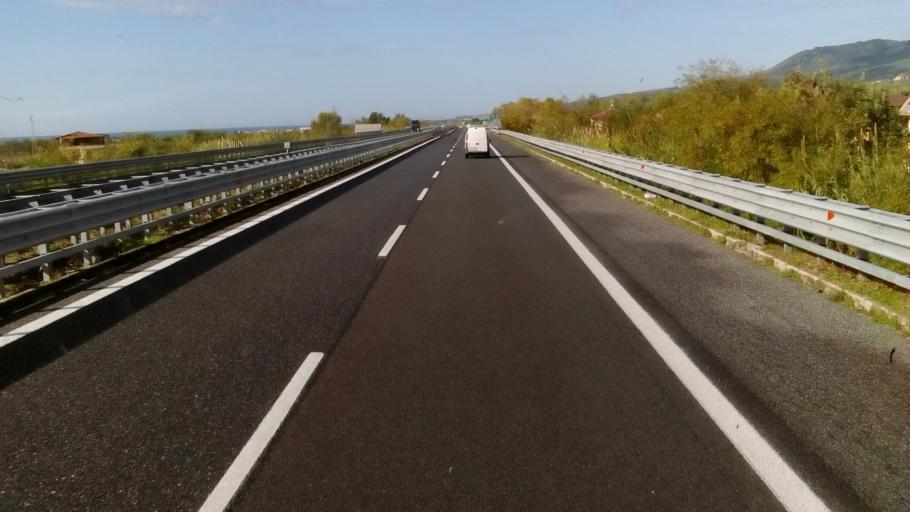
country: IT
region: Calabria
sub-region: Provincia di Catanzaro
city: Santa Eufemia Lamezia
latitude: 38.9270
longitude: 16.2472
